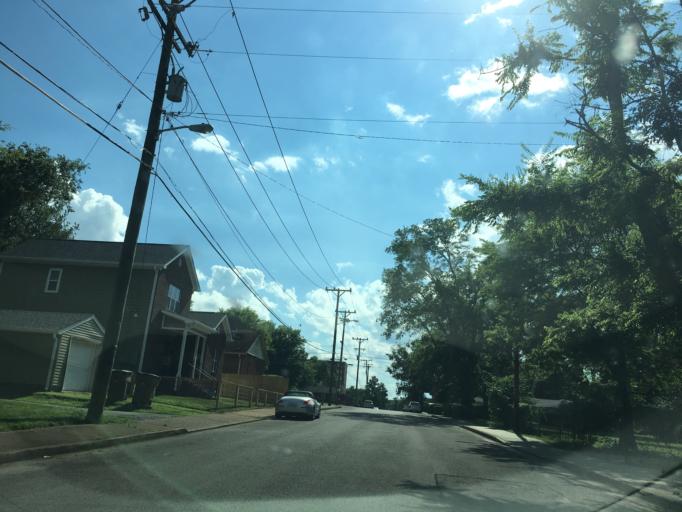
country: US
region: Tennessee
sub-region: Davidson County
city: Nashville
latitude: 36.1651
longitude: -86.8243
